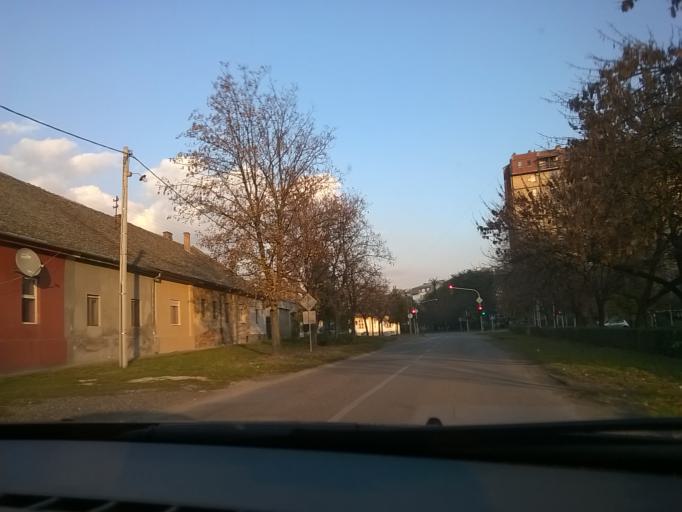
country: RS
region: Autonomna Pokrajina Vojvodina
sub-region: Juznobanatski Okrug
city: Pancevo
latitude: 44.8646
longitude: 20.6403
